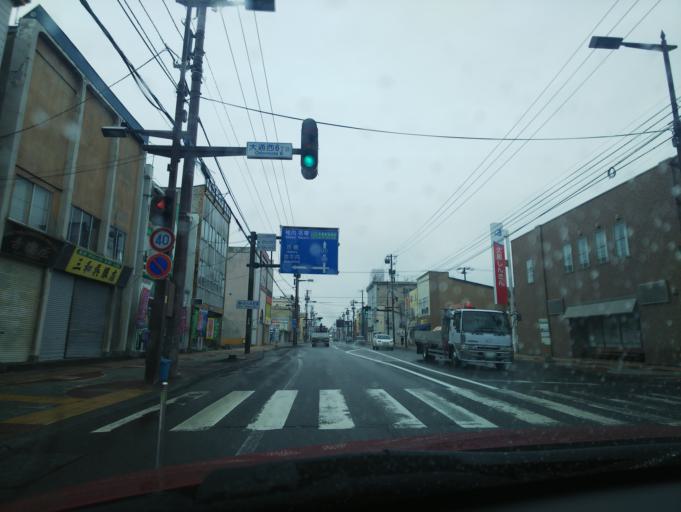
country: JP
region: Hokkaido
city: Nayoro
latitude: 44.1751
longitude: 142.3925
